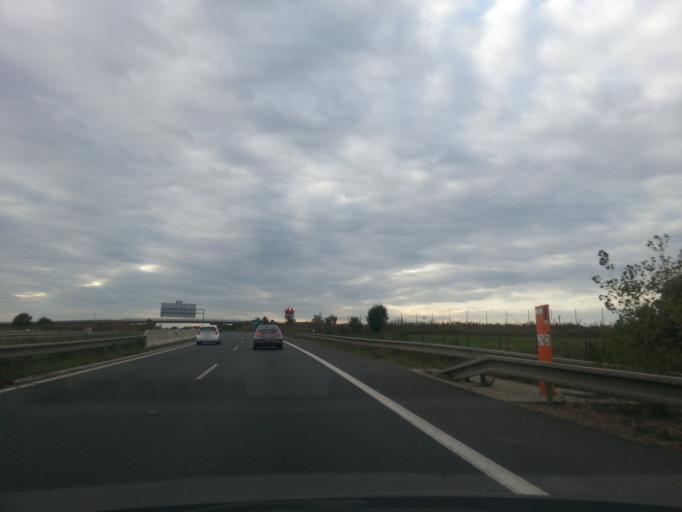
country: CZ
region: Central Bohemia
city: Hostivice
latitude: 50.0841
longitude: 14.2786
